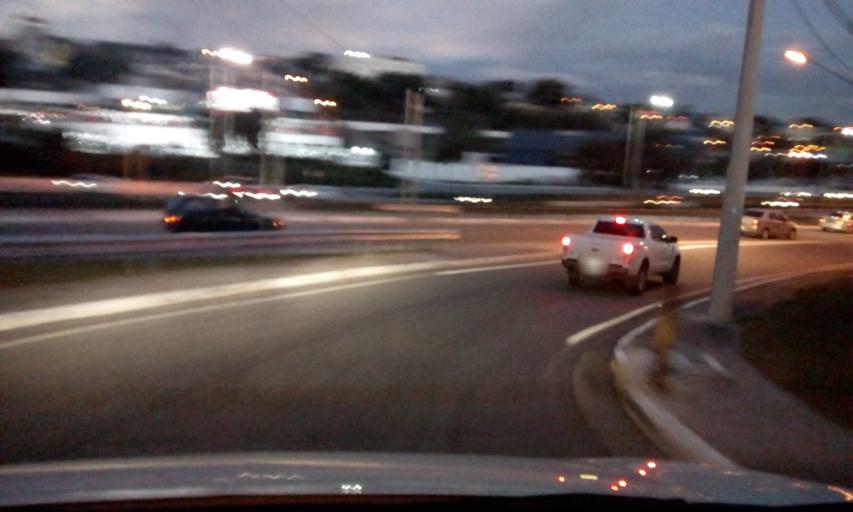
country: BR
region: Sao Paulo
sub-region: Sao Jose Dos Campos
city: Sao Jose dos Campos
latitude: -23.2128
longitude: -45.8916
